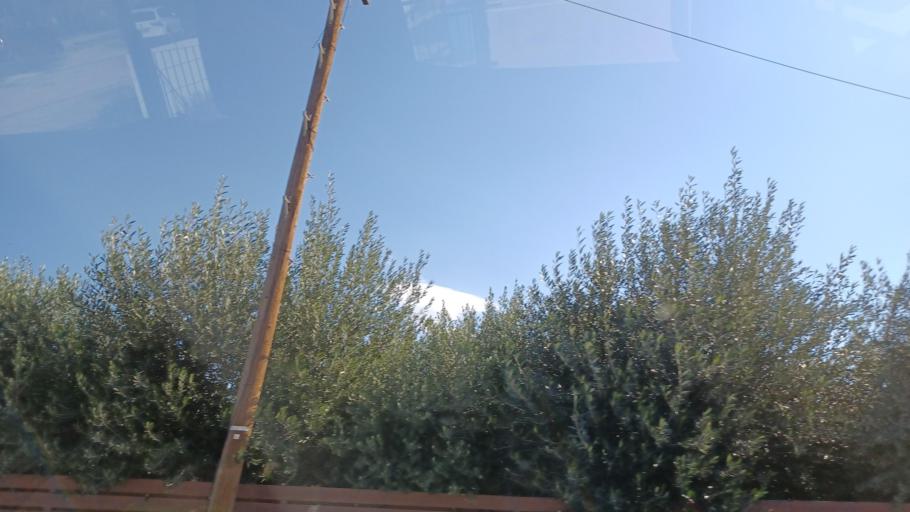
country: CY
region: Pafos
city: Paphos
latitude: 34.7618
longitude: 32.4525
